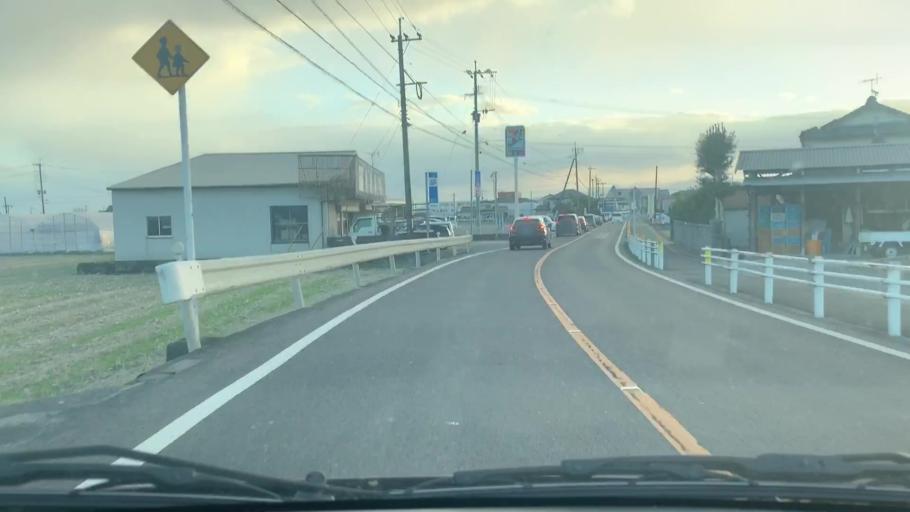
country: JP
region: Saga Prefecture
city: Saga-shi
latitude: 33.1876
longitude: 130.1933
